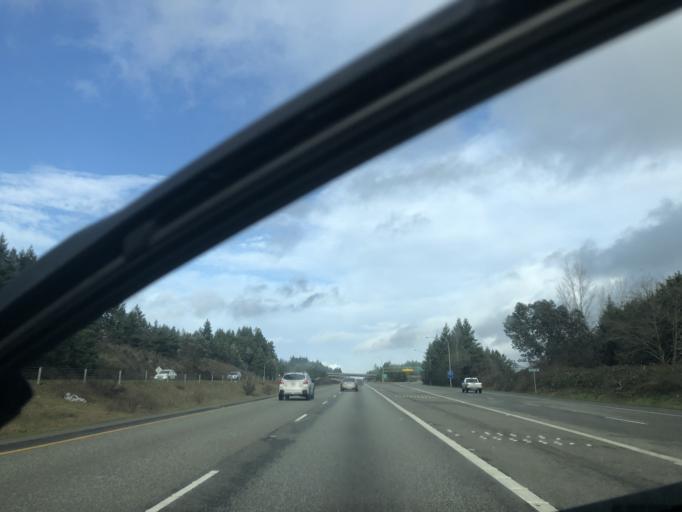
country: US
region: Washington
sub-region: Kitsap County
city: Bangor Trident Base
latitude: 47.6949
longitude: -122.6865
